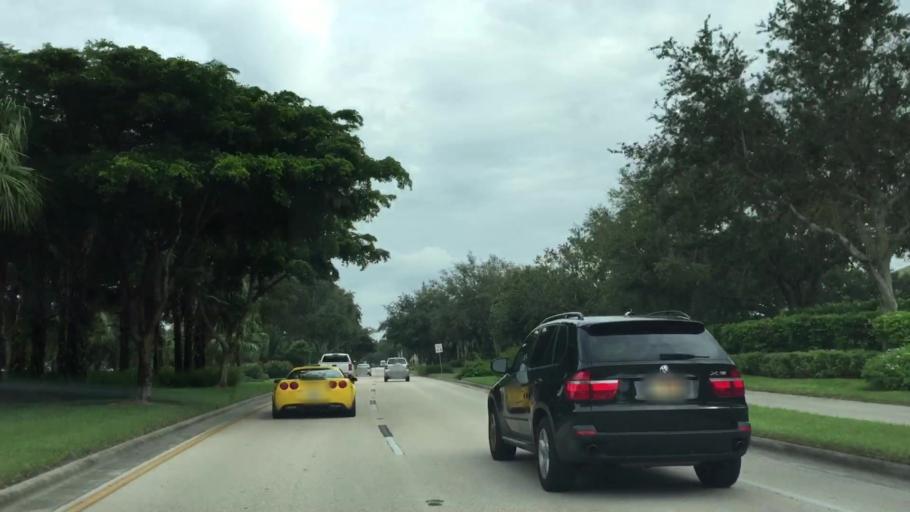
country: US
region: Florida
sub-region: Lee County
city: Estero
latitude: 26.3979
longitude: -81.7977
